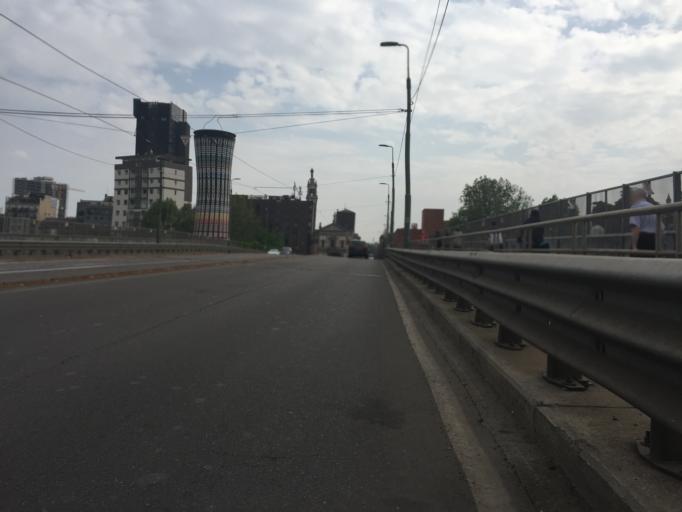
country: IT
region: Lombardy
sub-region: Citta metropolitana di Milano
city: Milano
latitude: 45.4877
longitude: 9.1822
